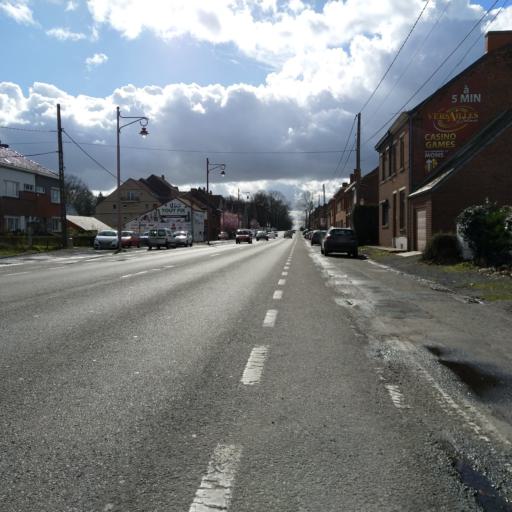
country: BE
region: Wallonia
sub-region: Province du Hainaut
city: Mons
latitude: 50.4889
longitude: 3.9427
